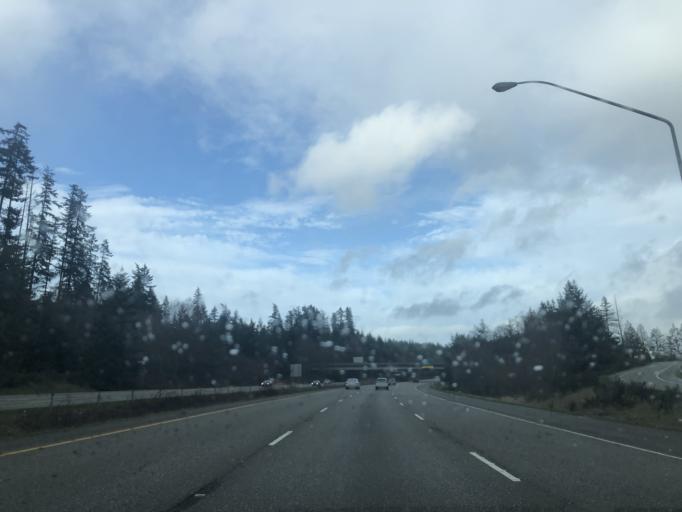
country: US
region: Washington
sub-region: Kitsap County
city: Silverdale
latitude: 47.6760
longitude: -122.6907
